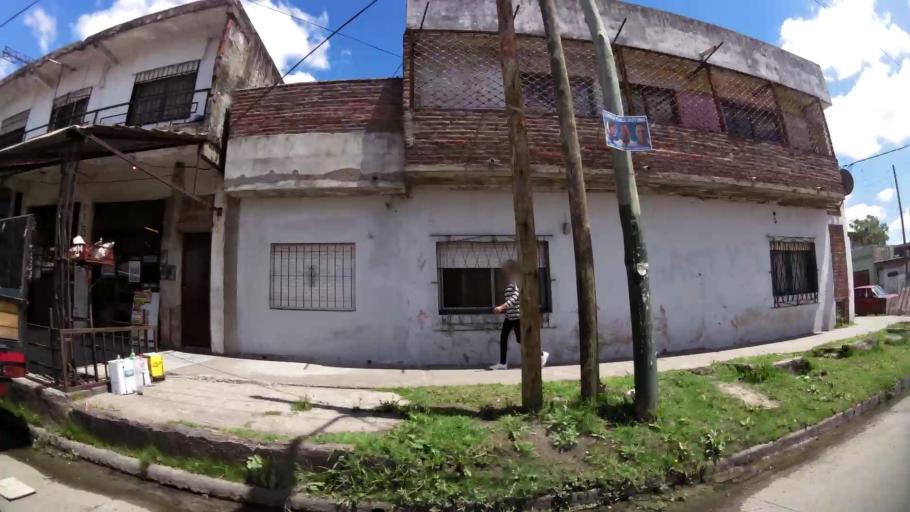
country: AR
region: Buenos Aires
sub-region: Partido de Lanus
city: Lanus
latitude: -34.7171
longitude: -58.4320
